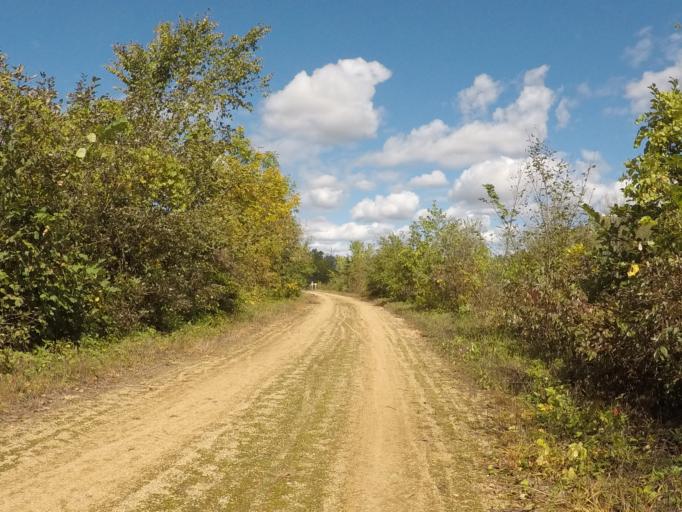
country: US
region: Wisconsin
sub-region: Richland County
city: Richland Center
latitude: 43.2612
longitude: -90.3017
